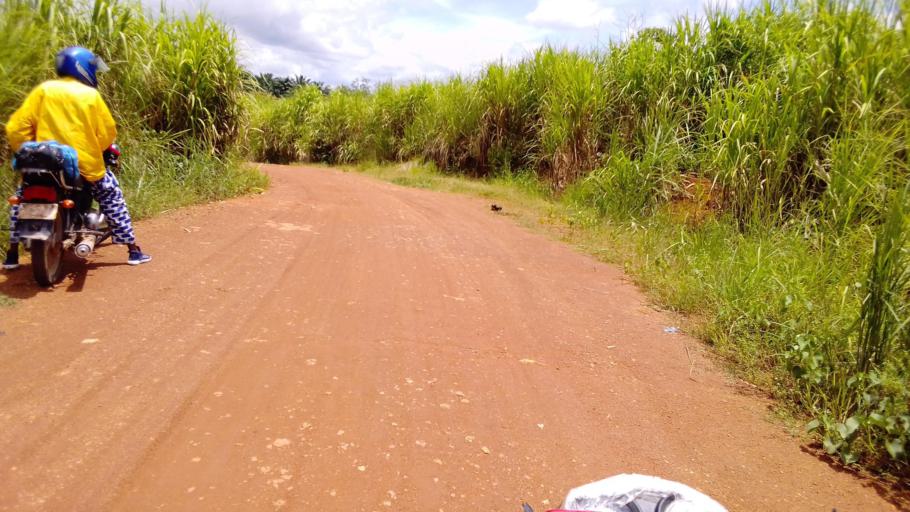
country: SL
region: Eastern Province
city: Koidu
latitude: 8.6726
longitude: -10.9393
